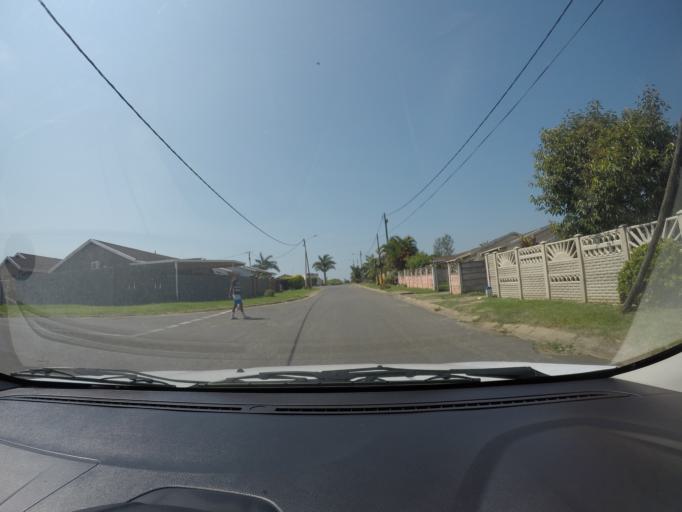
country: ZA
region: KwaZulu-Natal
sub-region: uThungulu District Municipality
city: eSikhawini
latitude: -28.8679
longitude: 31.9141
